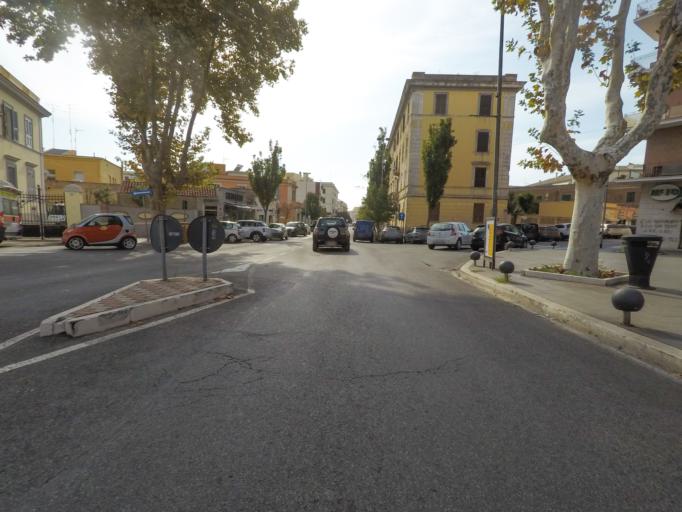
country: IT
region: Latium
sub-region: Citta metropolitana di Roma Capitale
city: Civitavecchia
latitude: 42.0931
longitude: 11.7968
